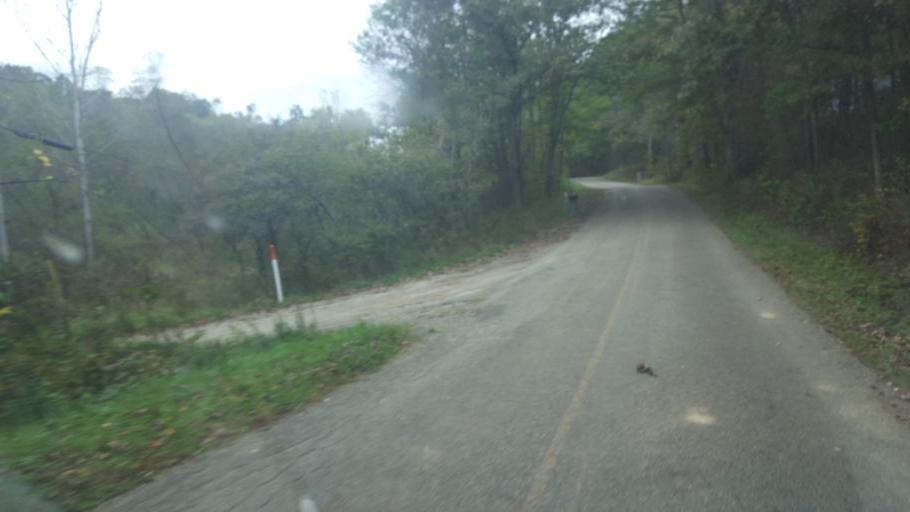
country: US
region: Ohio
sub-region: Carroll County
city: Carrollton
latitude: 40.4726
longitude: -81.1471
